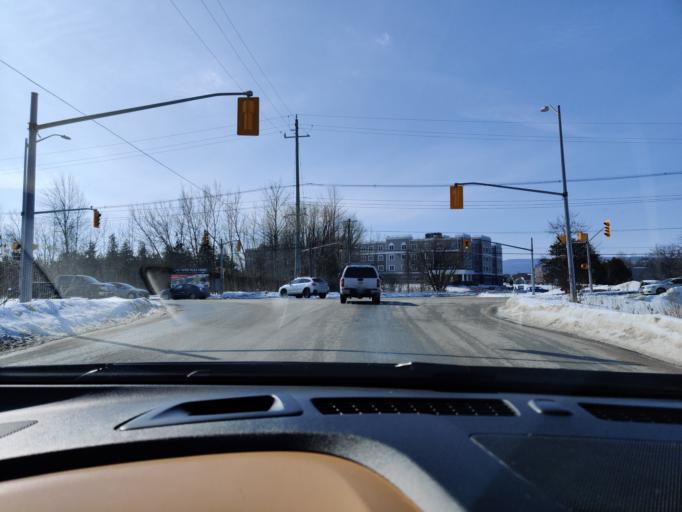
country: CA
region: Ontario
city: Collingwood
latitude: 44.5085
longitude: -80.2371
